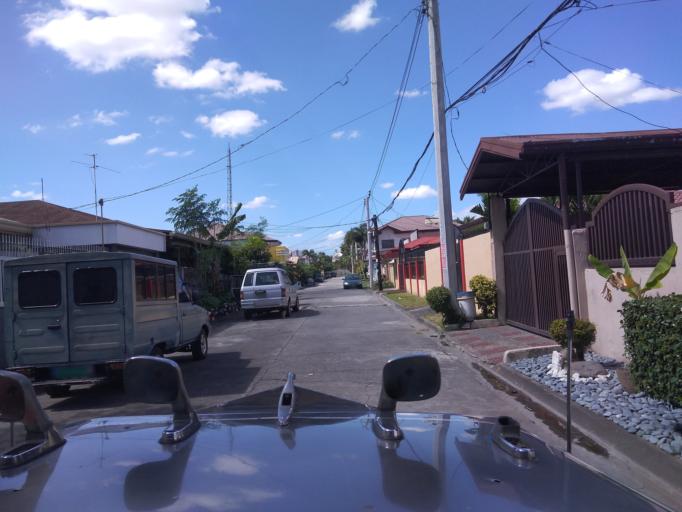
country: PH
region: Central Luzon
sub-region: Province of Pampanga
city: Calibutbut
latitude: 15.1159
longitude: 120.6021
